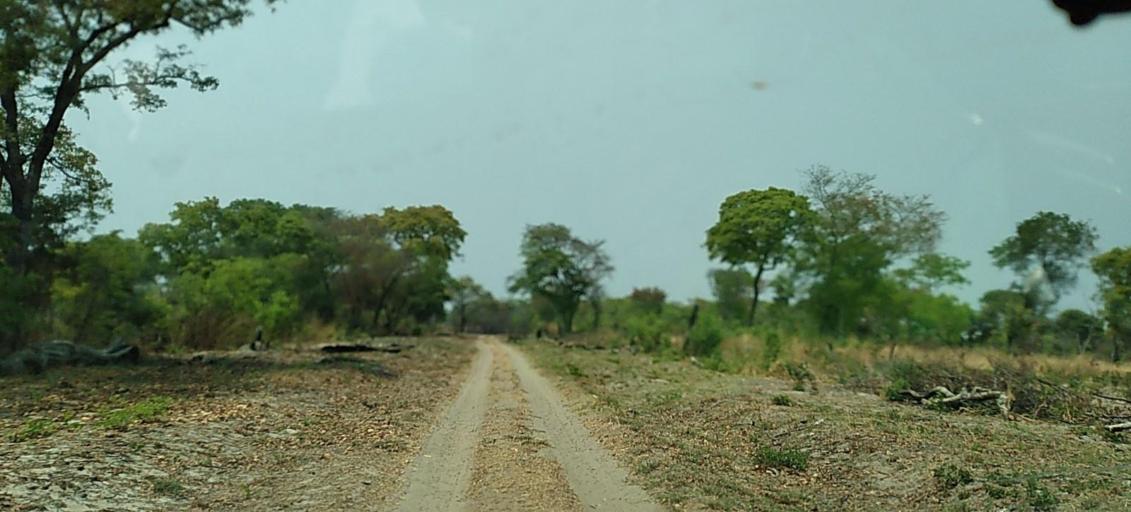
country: ZM
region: Western
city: Lukulu
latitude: -13.9624
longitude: 23.2255
